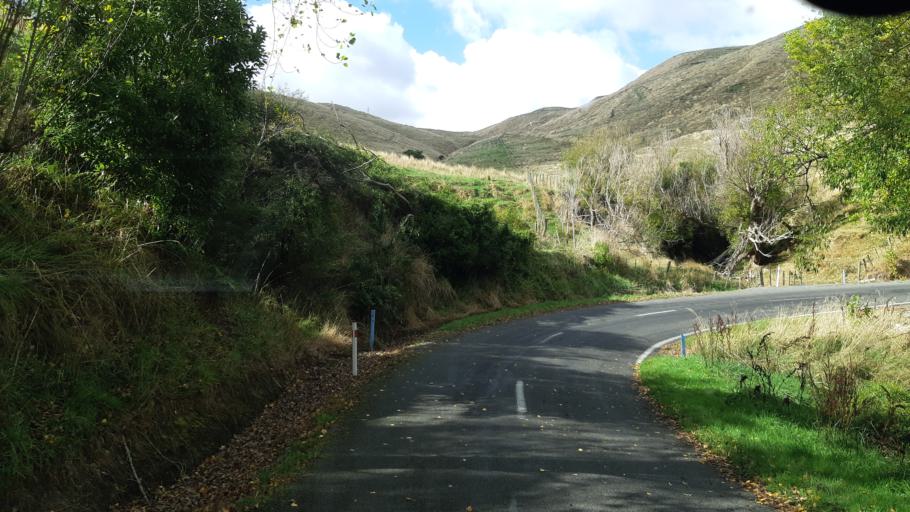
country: NZ
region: Manawatu-Wanganui
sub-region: Ruapehu District
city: Waiouru
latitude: -39.7194
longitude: 175.6767
